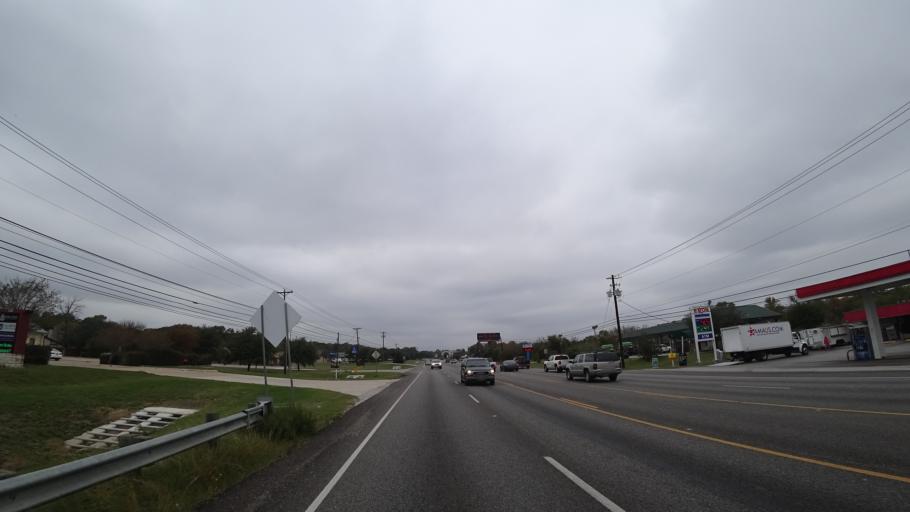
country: US
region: Texas
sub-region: Travis County
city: Barton Creek
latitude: 30.2365
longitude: -97.8779
